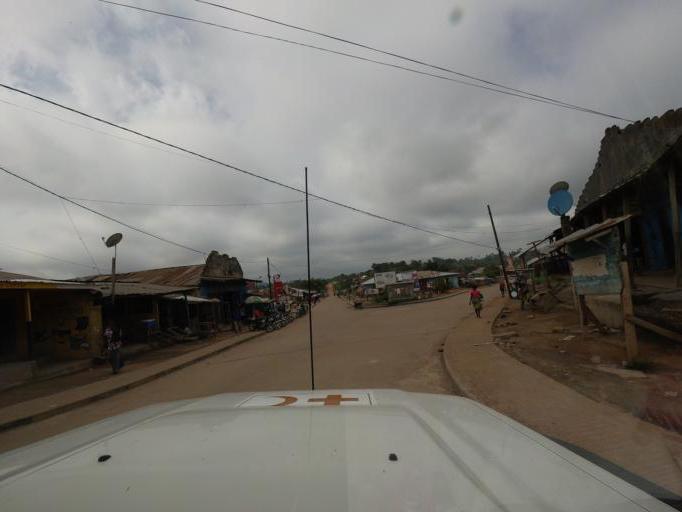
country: LR
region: Lofa
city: Voinjama
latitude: 8.4222
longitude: -9.7527
